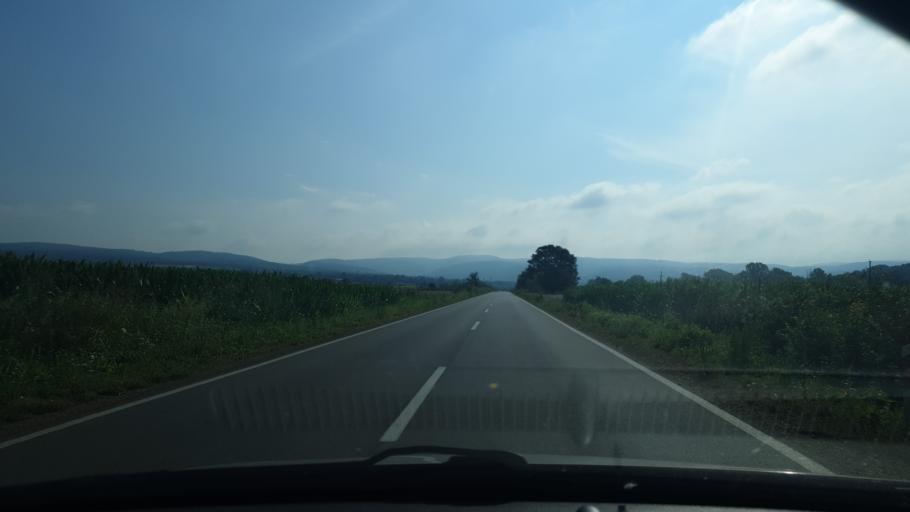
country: RS
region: Central Serbia
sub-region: Pomoravski Okrug
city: Cuprija
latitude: 43.9507
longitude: 21.4401
